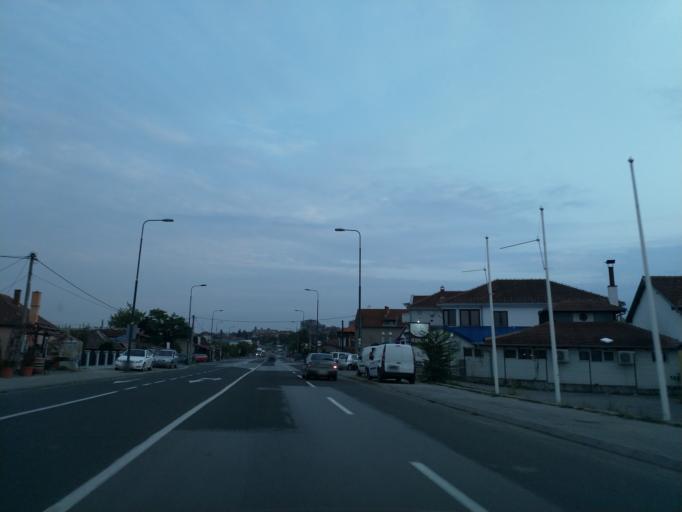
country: RS
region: Central Serbia
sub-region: Sumadijski Okrug
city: Kragujevac
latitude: 44.0406
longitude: 20.9101
